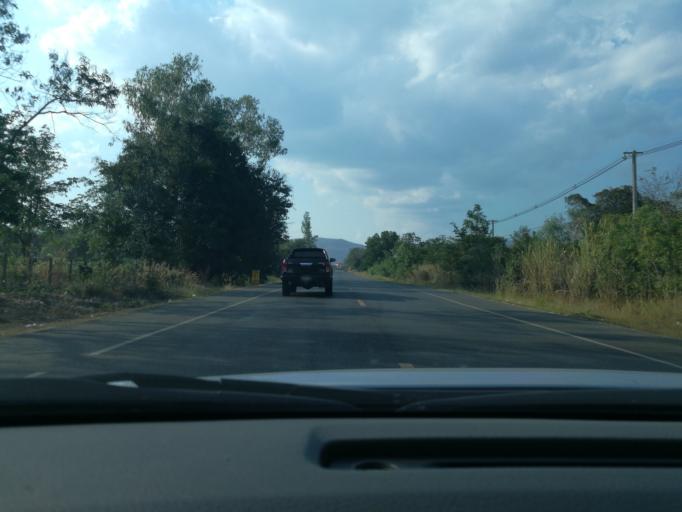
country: TH
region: Phetchabun
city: Phetchabun
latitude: 16.5425
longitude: 101.1471
